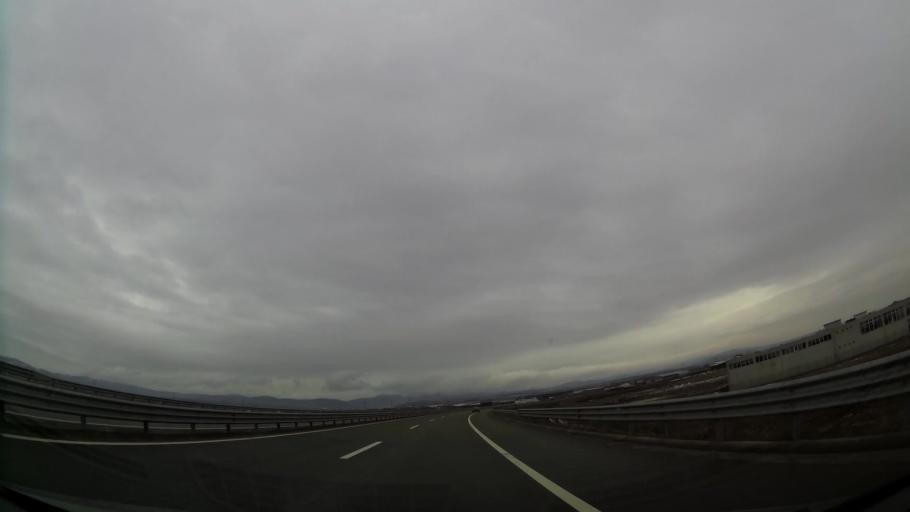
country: XK
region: Pristina
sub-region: Lipjan
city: Lipljan
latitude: 42.5303
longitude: 21.1610
